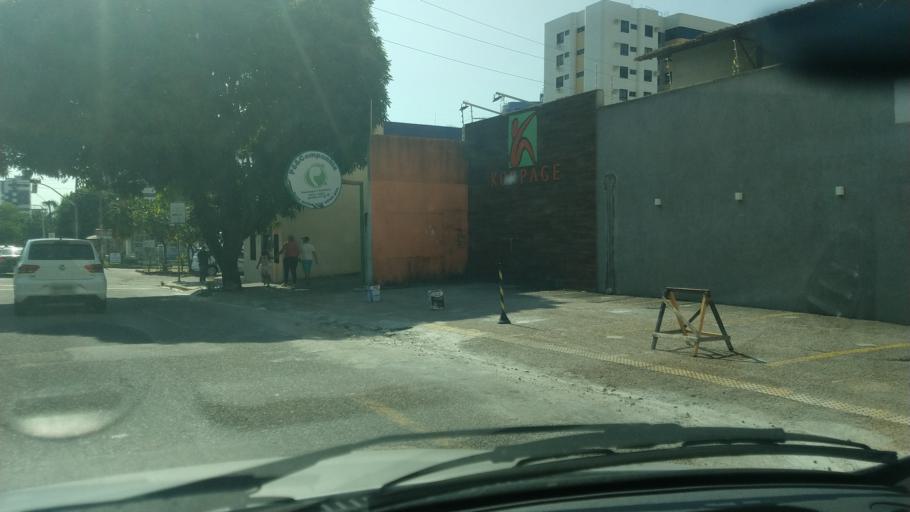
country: BR
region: Rio Grande do Norte
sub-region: Natal
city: Natal
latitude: -5.8005
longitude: -35.2028
